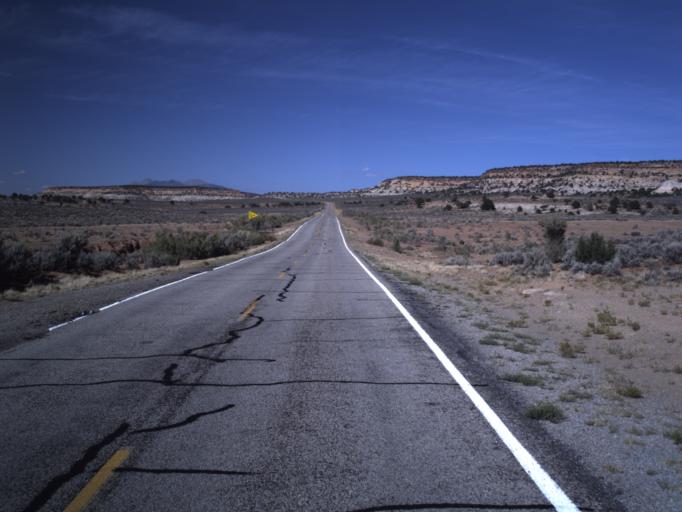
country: US
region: Utah
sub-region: San Juan County
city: Monticello
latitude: 38.0274
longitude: -109.4234
